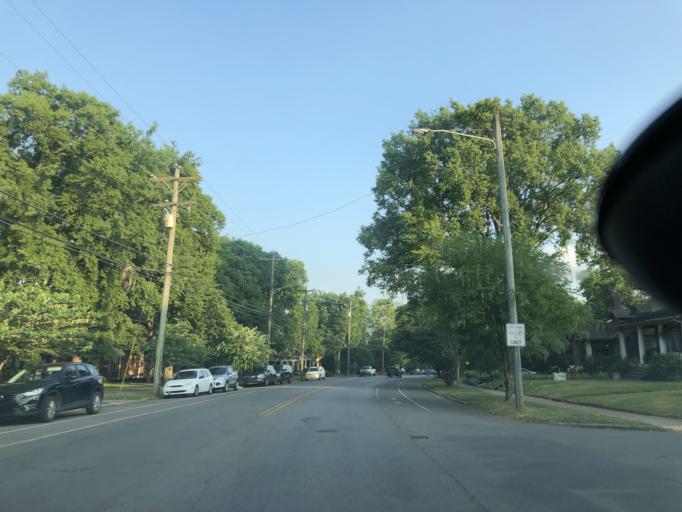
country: US
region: Tennessee
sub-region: Davidson County
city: Nashville
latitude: 36.1276
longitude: -86.7944
